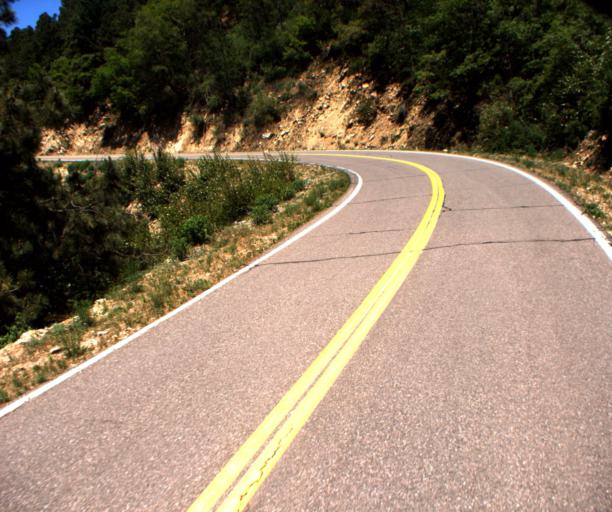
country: US
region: Arizona
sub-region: Graham County
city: Swift Trail Junction
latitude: 32.6439
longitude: -109.8503
